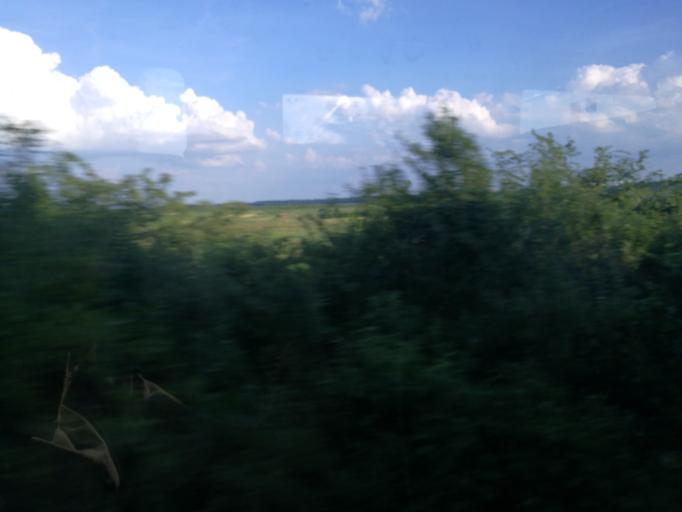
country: RO
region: Arges
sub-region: Oras Stefanesti
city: Golesti
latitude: 44.8363
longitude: 24.9428
